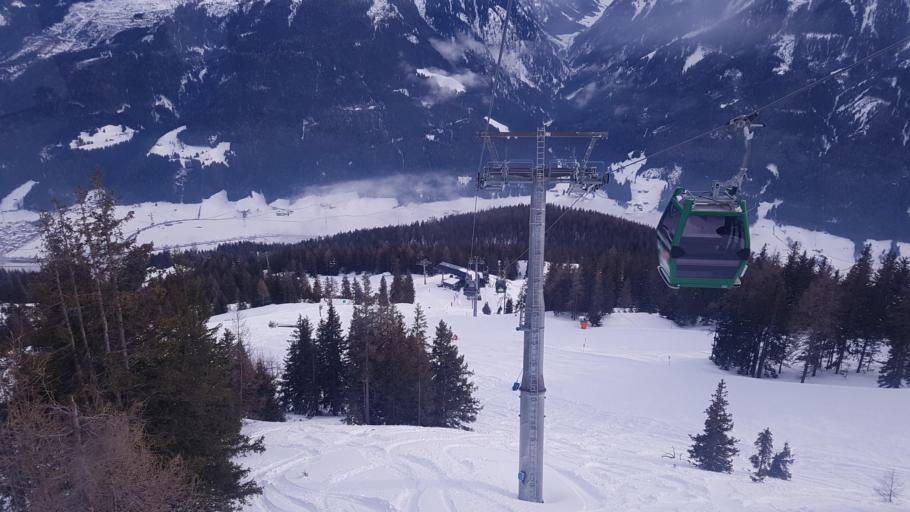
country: AT
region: Salzburg
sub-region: Politischer Bezirk Zell am See
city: Neukirchen am Grossvenediger
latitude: 47.2753
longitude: 12.3006
